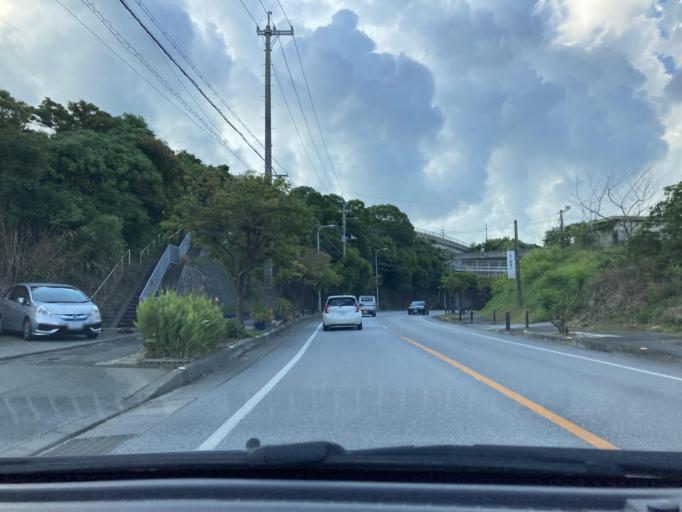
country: JP
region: Okinawa
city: Tomigusuku
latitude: 26.1819
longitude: 127.7258
